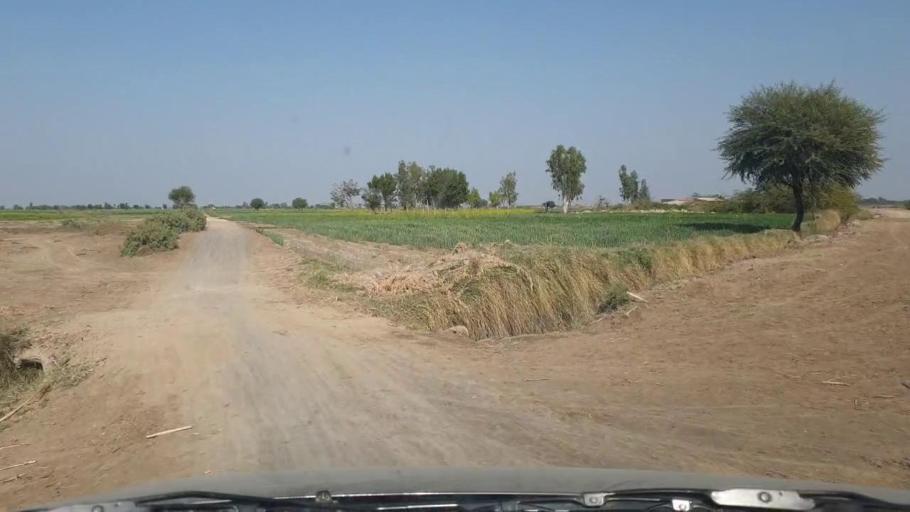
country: PK
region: Sindh
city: Samaro
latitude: 25.1653
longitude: 69.3278
